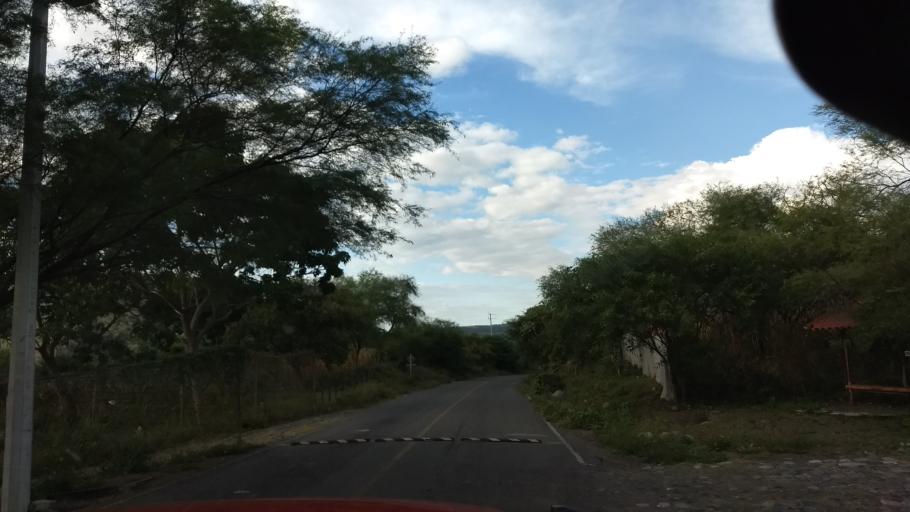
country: MX
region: Colima
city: Suchitlan
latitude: 19.4561
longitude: -103.8263
